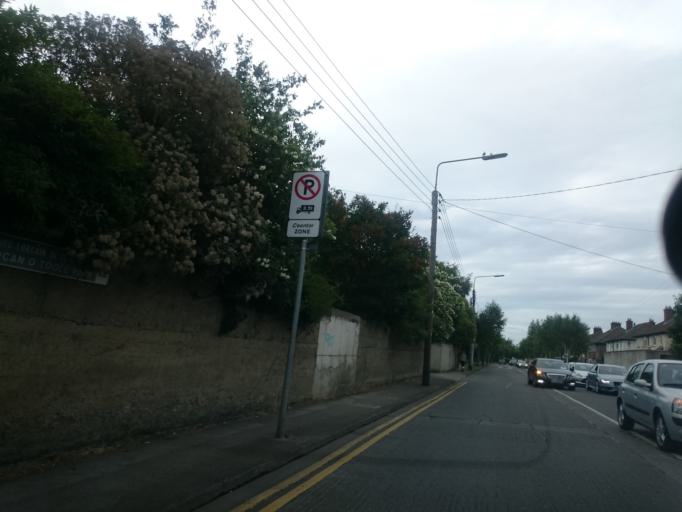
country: IE
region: Leinster
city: Templeogue
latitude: 53.3140
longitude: -6.3096
